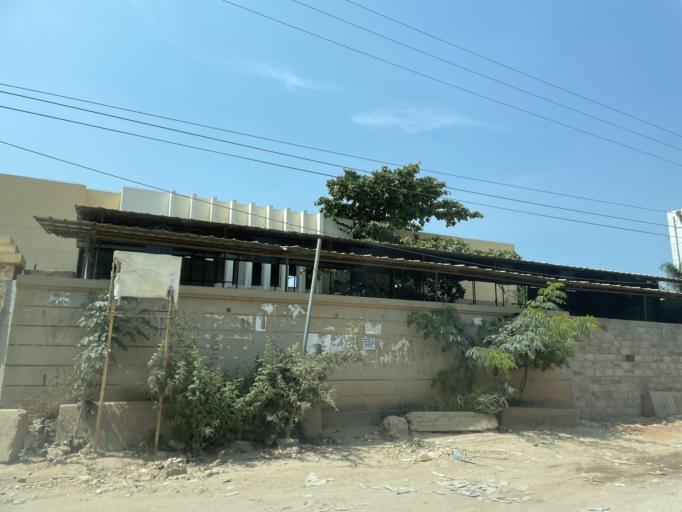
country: AO
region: Luanda
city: Luanda
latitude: -8.9010
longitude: 13.1821
